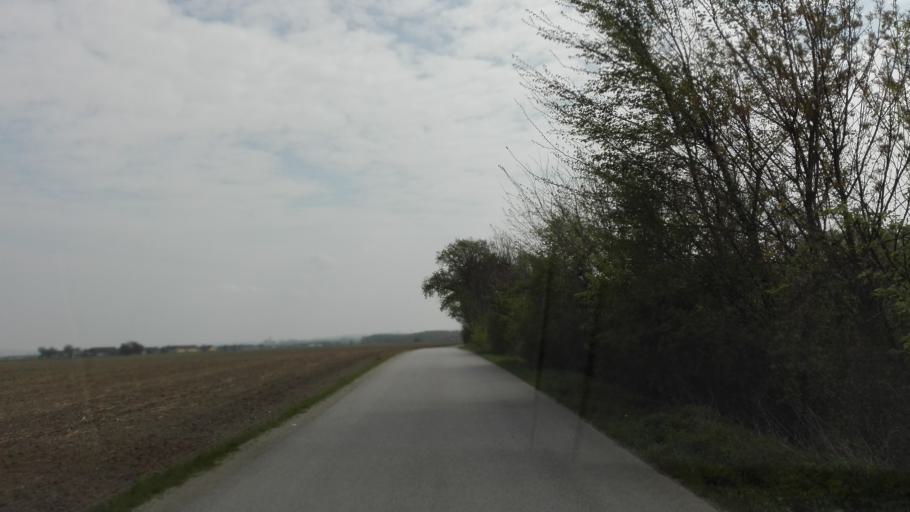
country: AT
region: Lower Austria
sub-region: Politischer Bezirk Amstetten
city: Strengberg
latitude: 48.1911
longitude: 14.6385
